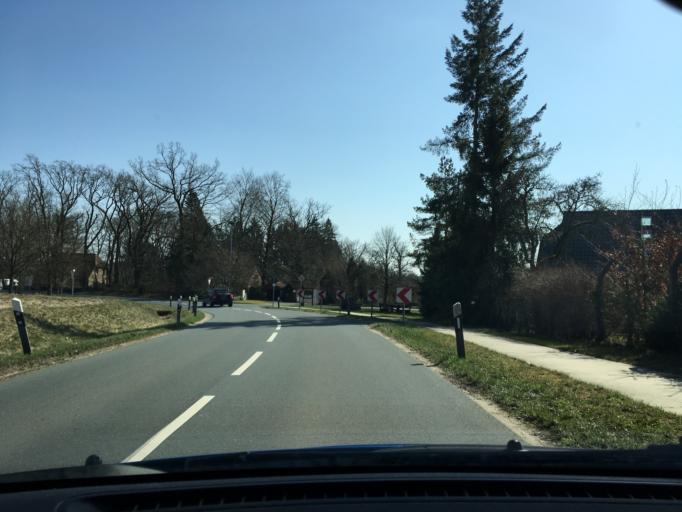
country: DE
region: Lower Saxony
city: Eimke
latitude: 52.9755
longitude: 10.3098
